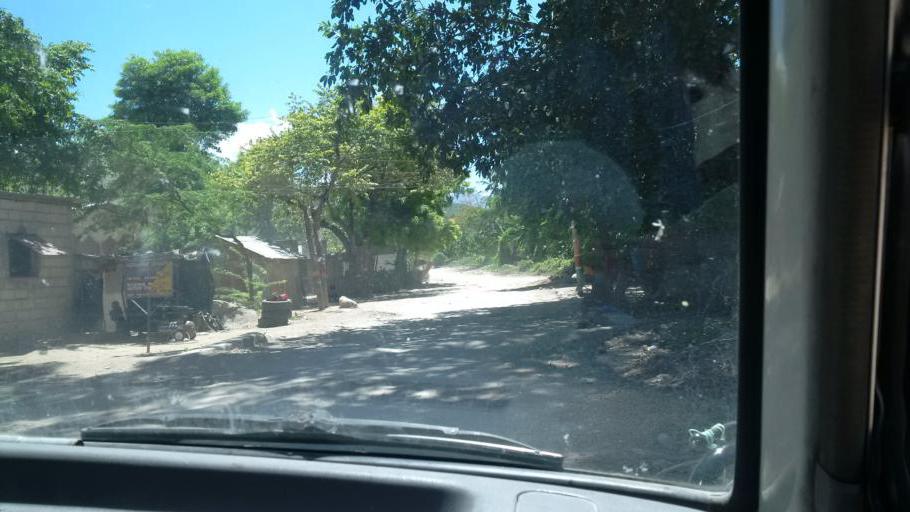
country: HT
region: Ouest
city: Thomazeau
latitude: 18.6567
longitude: -72.1364
